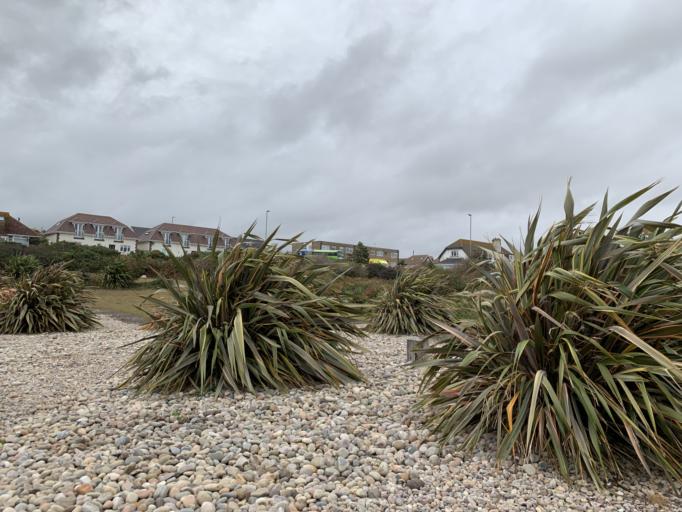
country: GB
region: England
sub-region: East Sussex
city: Peacehaven
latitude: 50.7925
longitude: -0.0094
